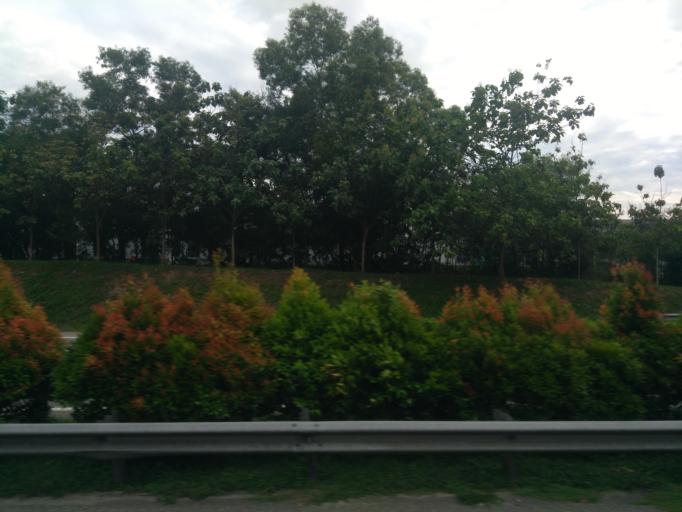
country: MY
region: Melaka
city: Pulau Sebang
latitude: 2.4265
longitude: 102.2106
